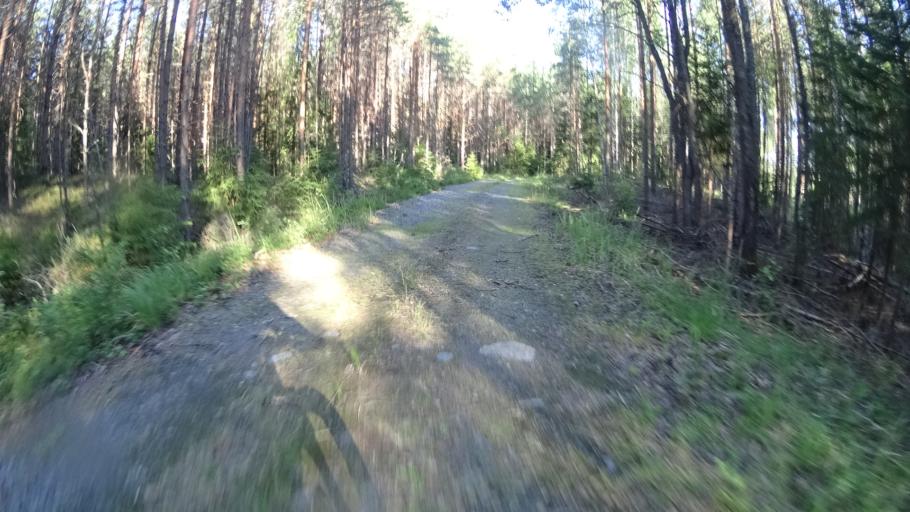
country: FI
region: Uusimaa
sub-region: Helsinki
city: Karkkila
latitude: 60.6623
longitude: 24.1335
